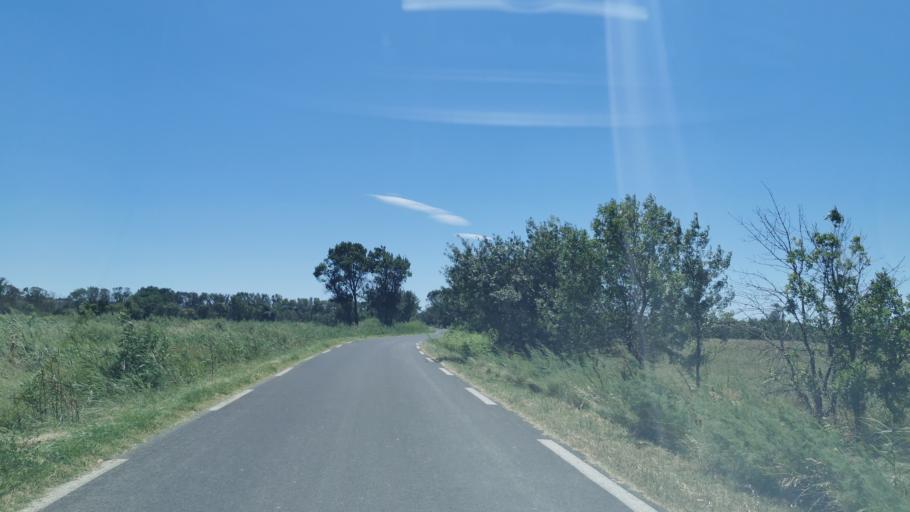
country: FR
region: Languedoc-Roussillon
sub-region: Departement de l'Herault
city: Nissan-lez-Enserune
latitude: 43.2655
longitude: 3.1208
